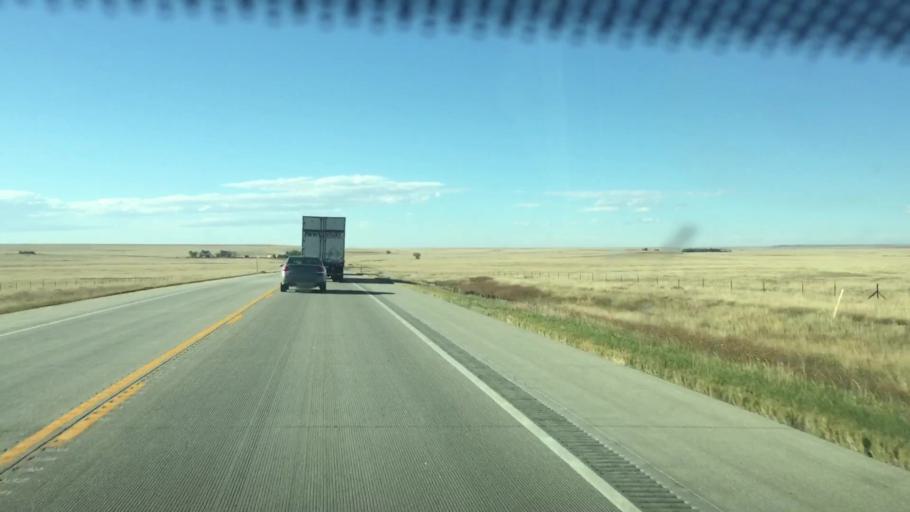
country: US
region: Colorado
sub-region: Lincoln County
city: Hugo
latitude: 38.9250
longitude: -103.1906
